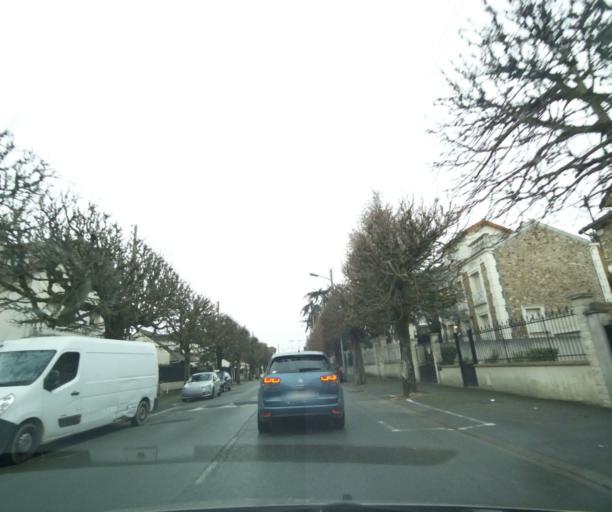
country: FR
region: Ile-de-France
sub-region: Departement du Val-de-Marne
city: Ablon-sur-Seine
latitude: 48.7322
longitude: 2.4183
